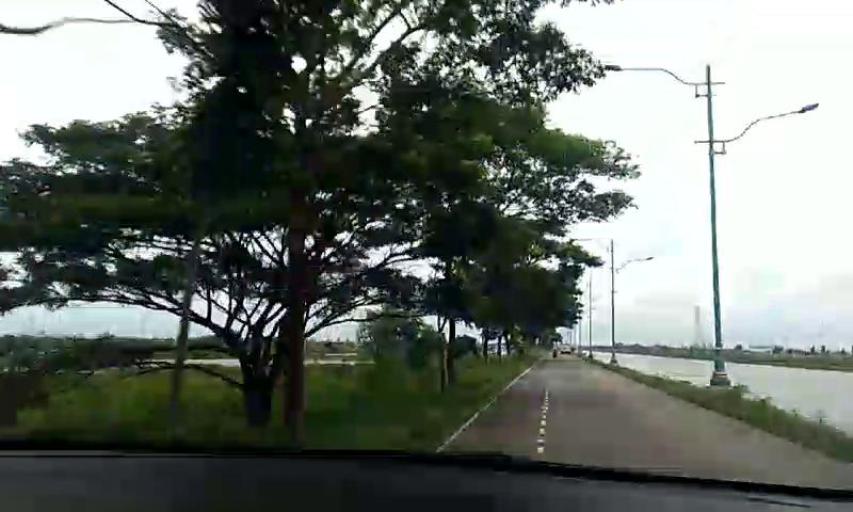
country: ID
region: West Java
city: Bekasi
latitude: -6.1240
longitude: 106.9692
